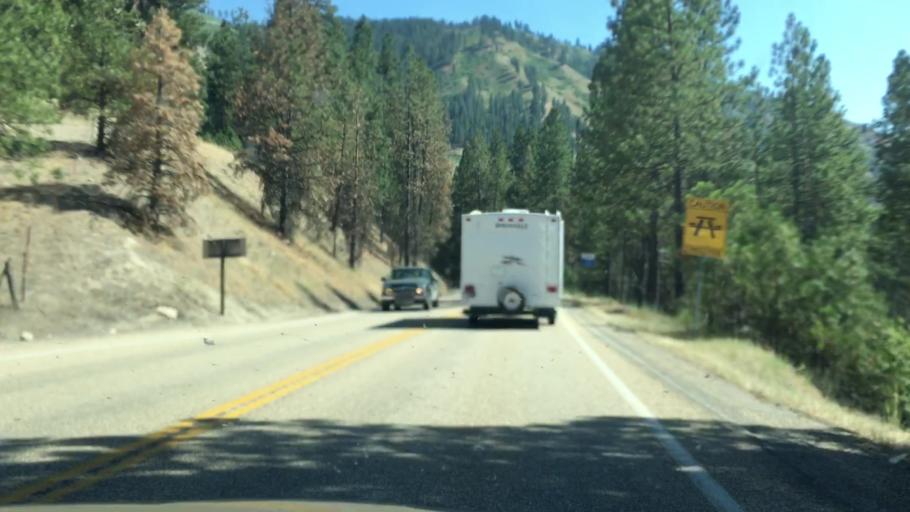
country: US
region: Idaho
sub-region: Boise County
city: Idaho City
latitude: 44.0759
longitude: -116.1205
